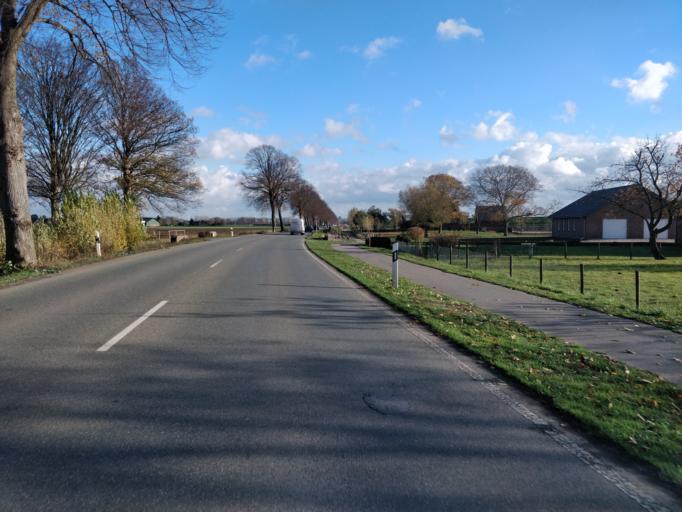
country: NL
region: Gelderland
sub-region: Oude IJsselstreek
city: Gendringen
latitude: 51.8192
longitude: 6.3457
